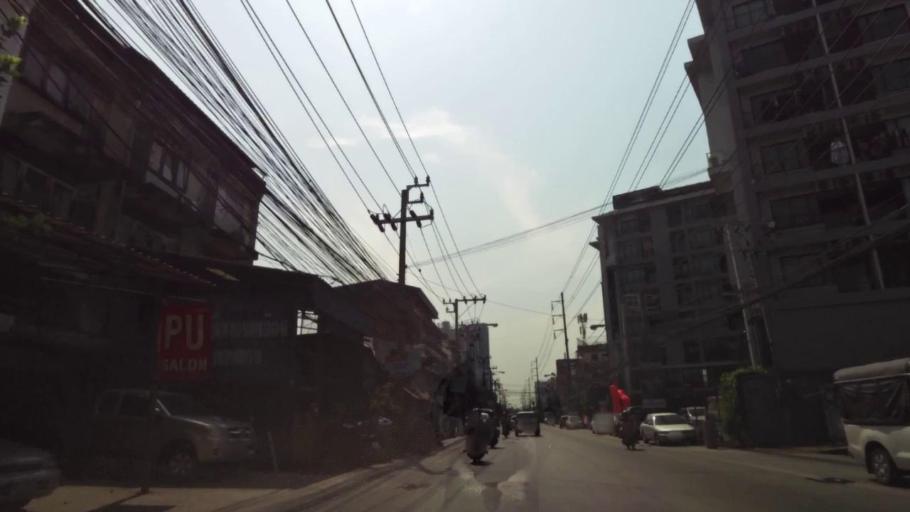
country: TH
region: Bangkok
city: Phra Khanong
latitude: 13.6534
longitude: 100.5931
